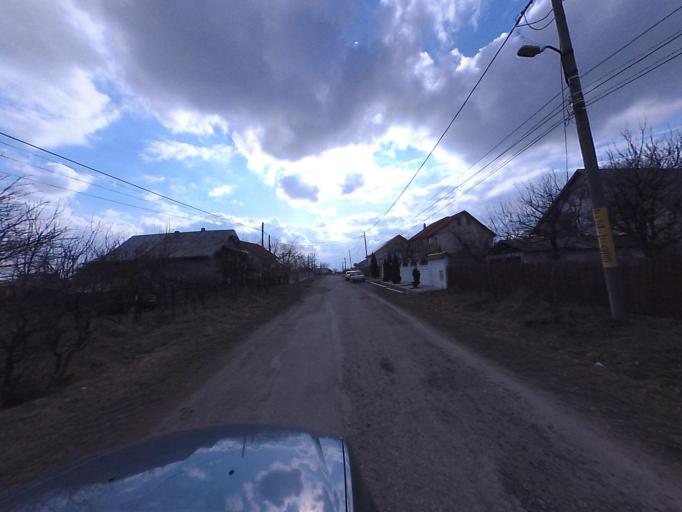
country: RO
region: Neamt
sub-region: Oras Targu Neamt
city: Targu Neamt
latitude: 47.2132
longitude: 26.3793
